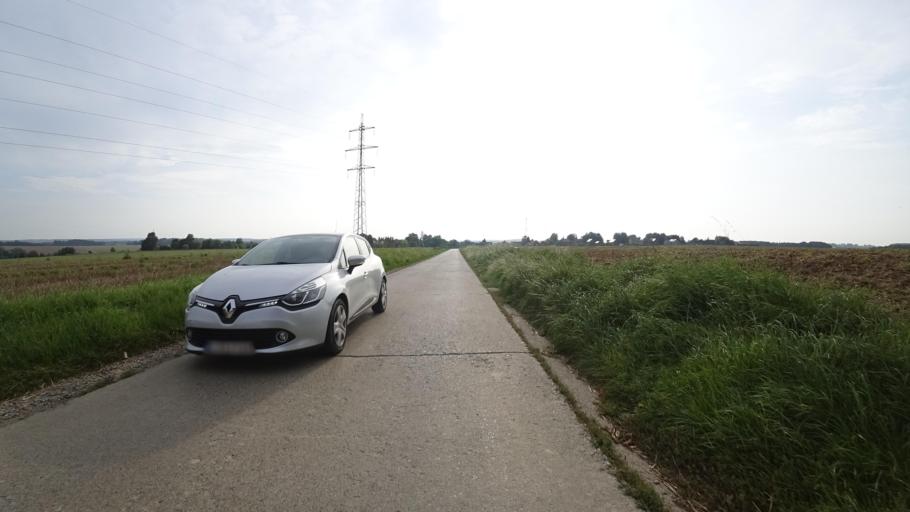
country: BE
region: Wallonia
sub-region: Province de Namur
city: Namur
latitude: 50.5223
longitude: 4.8328
